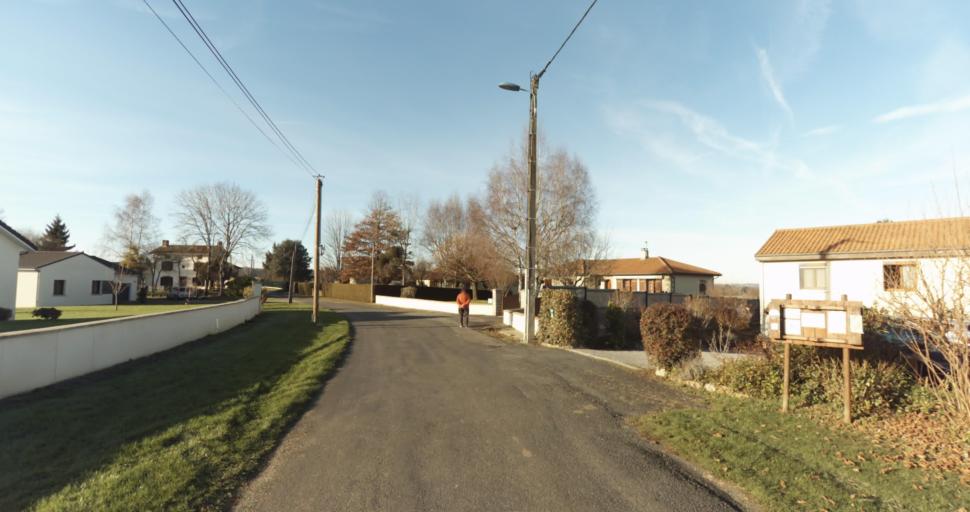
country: FR
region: Limousin
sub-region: Departement de la Haute-Vienne
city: Aixe-sur-Vienne
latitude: 45.7982
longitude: 1.1154
